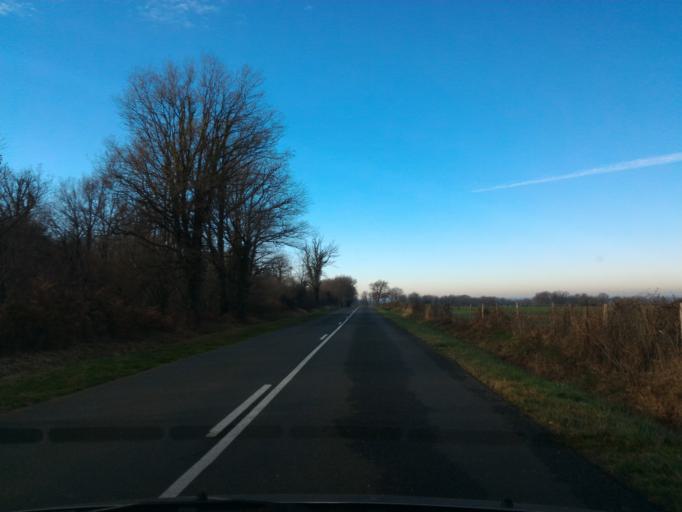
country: FR
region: Poitou-Charentes
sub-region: Departement de la Charente
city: Confolens
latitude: 46.0317
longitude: 0.5752
